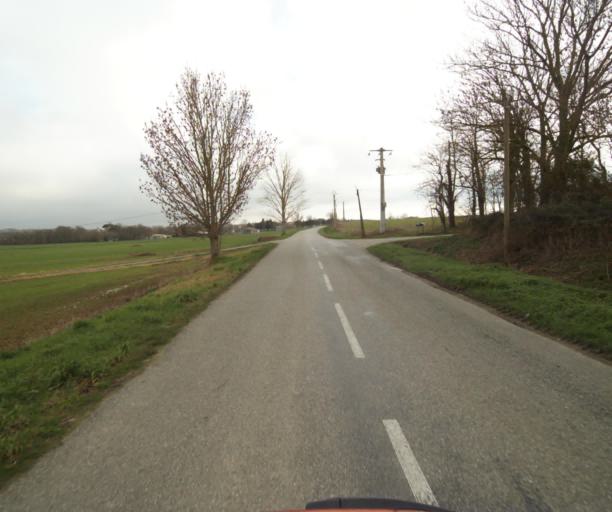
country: FR
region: Languedoc-Roussillon
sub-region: Departement de l'Aude
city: Belpech
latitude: 43.2058
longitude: 1.7312
